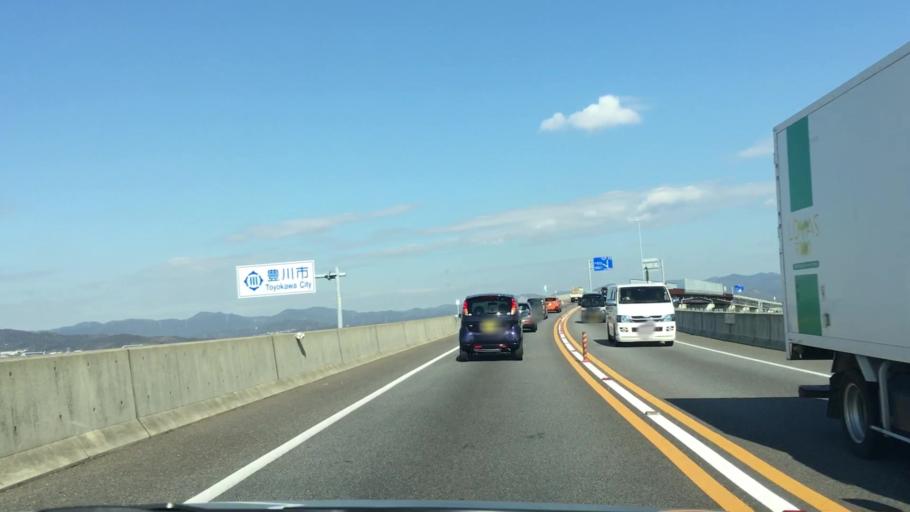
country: JP
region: Aichi
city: Kozakai-cho
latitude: 34.7943
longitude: 137.3309
